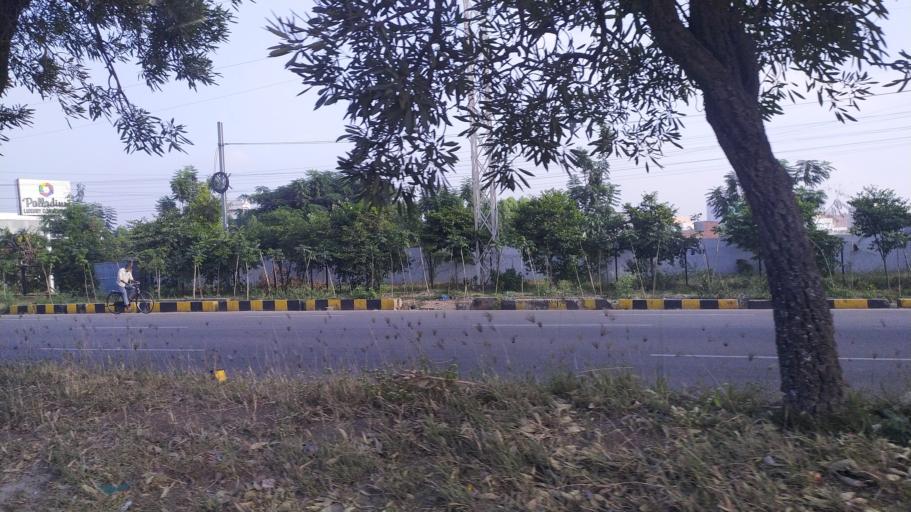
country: IN
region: Telangana
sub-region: Rangareddi
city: Balapur
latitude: 17.3171
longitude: 78.4391
